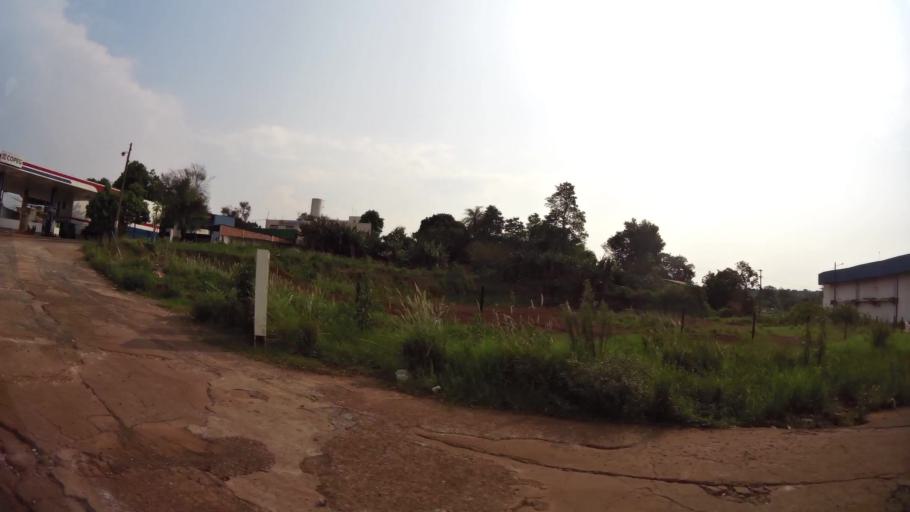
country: PY
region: Alto Parana
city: Ciudad del Este
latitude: -25.4927
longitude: -54.6619
